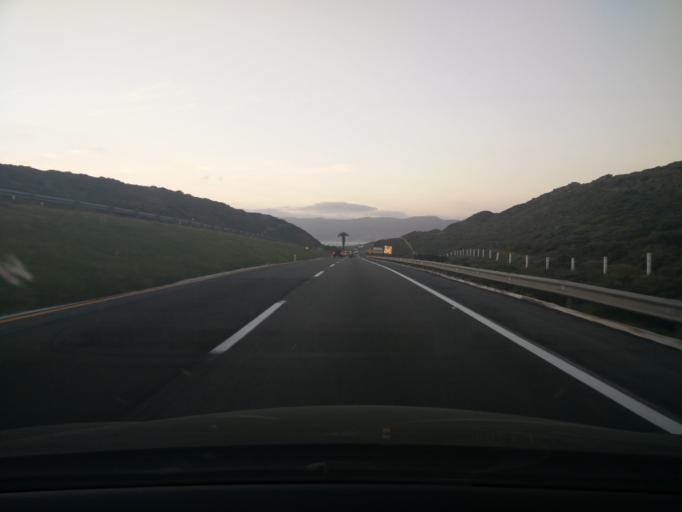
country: MX
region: Baja California
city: El Sauzal
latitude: 31.9130
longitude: -116.7521
